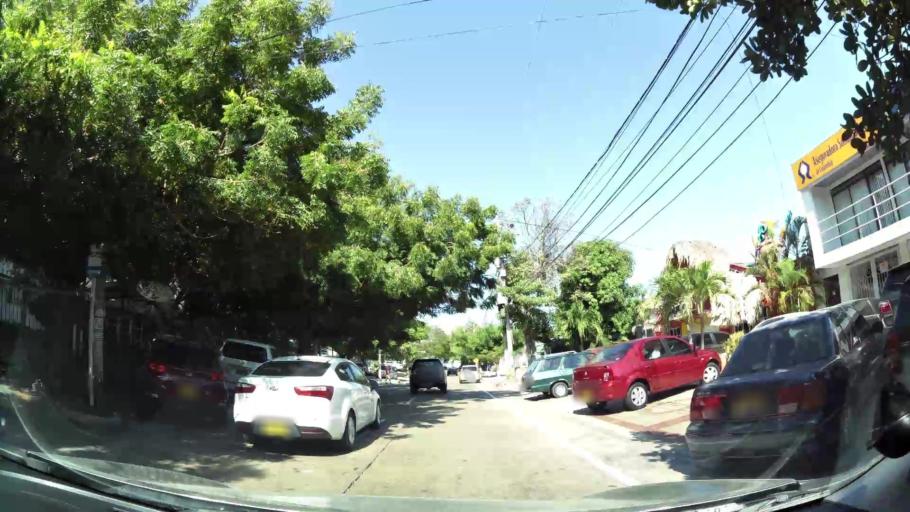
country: CO
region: Atlantico
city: Barranquilla
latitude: 10.9966
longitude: -74.8077
